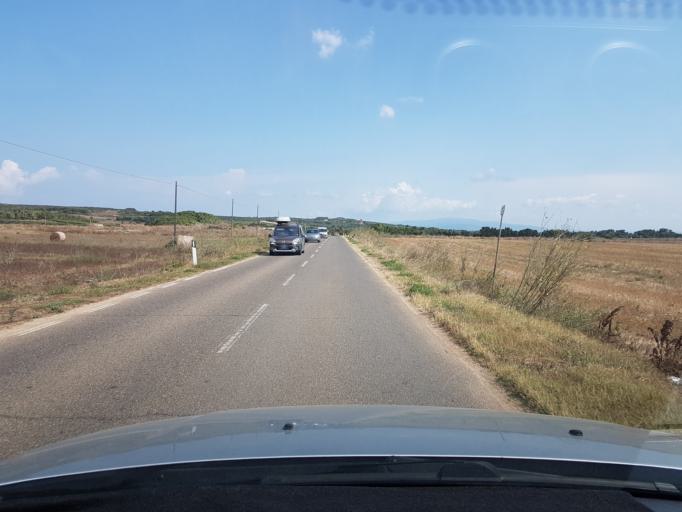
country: IT
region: Sardinia
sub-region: Provincia di Oristano
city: Cabras
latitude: 39.9079
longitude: 8.4384
